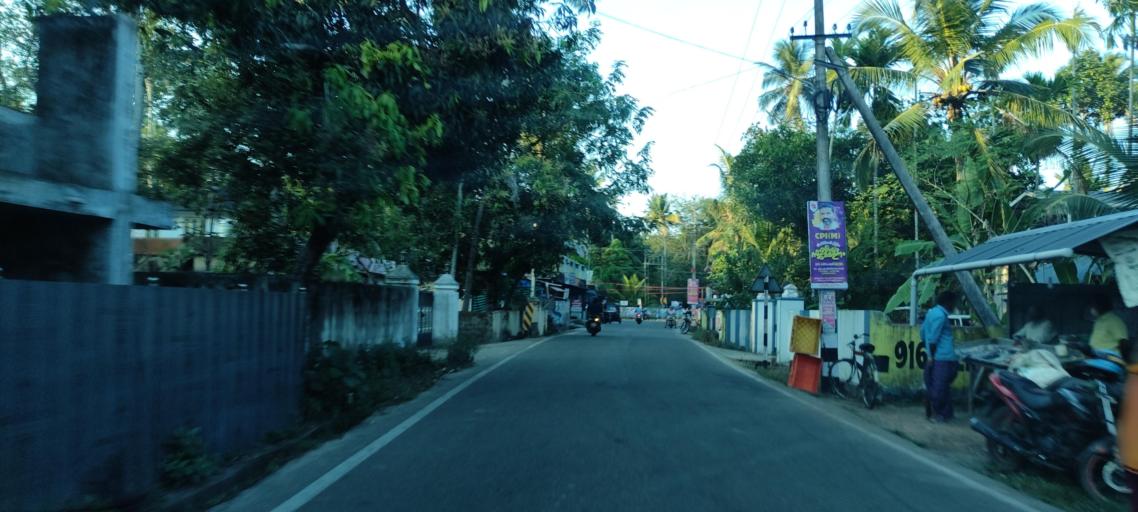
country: IN
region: Kerala
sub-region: Alappuzha
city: Kayankulam
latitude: 9.1895
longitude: 76.4715
